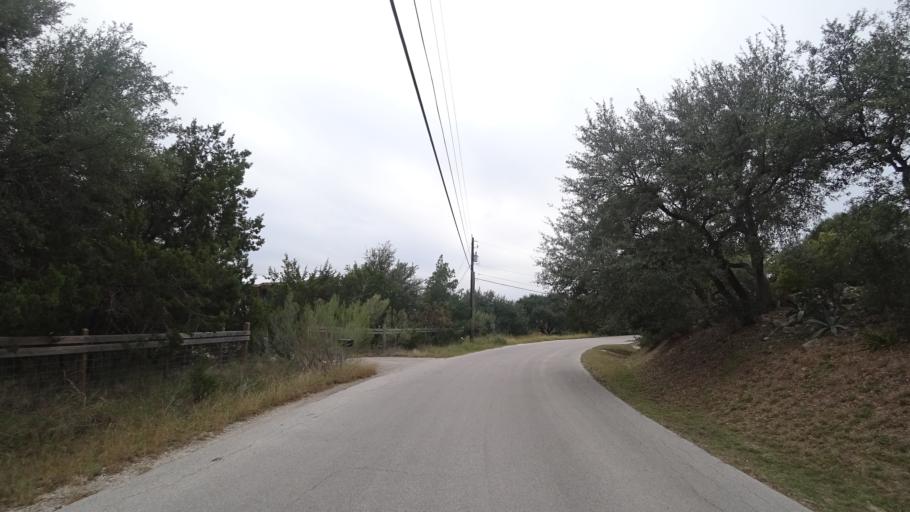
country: US
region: Texas
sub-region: Travis County
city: Hudson Bend
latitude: 30.3687
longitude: -97.9196
